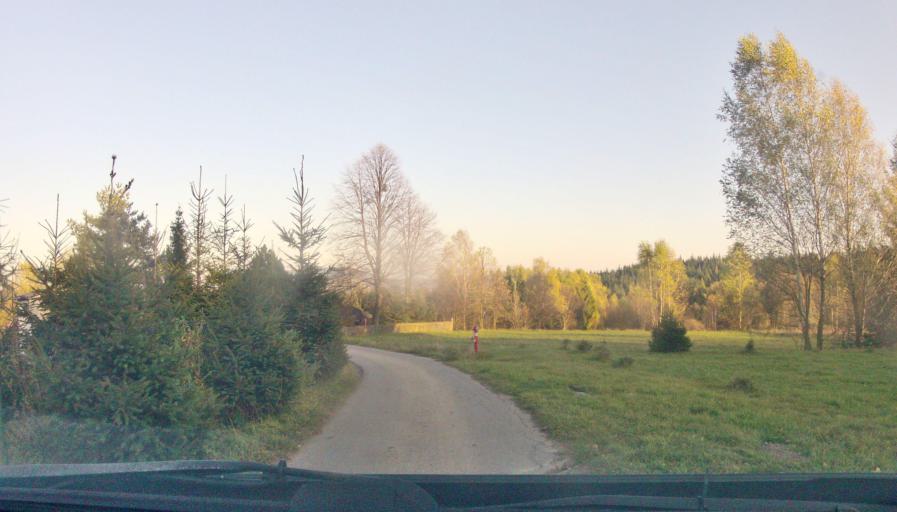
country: PL
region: Lesser Poland Voivodeship
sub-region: Powiat suski
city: Krzeszow
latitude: 49.7578
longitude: 19.4403
